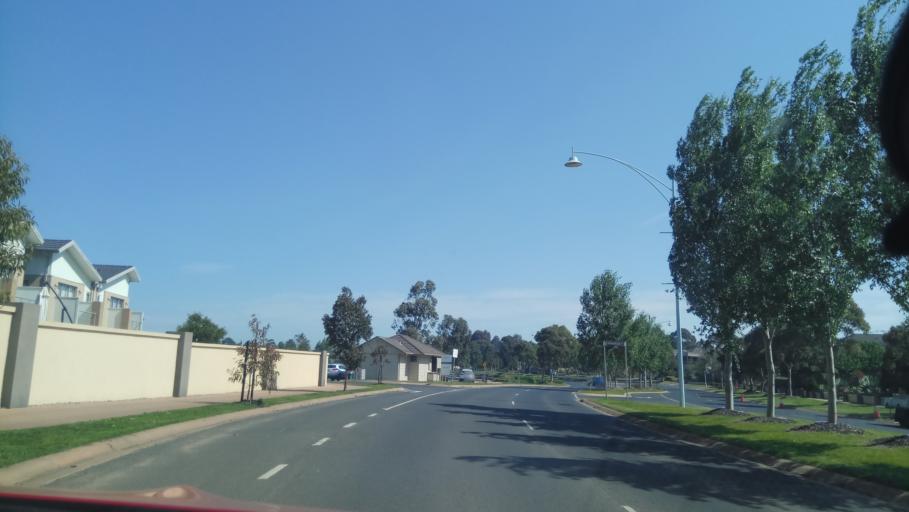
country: AU
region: Victoria
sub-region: Wyndham
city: Point Cook
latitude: -37.8946
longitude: 144.7596
